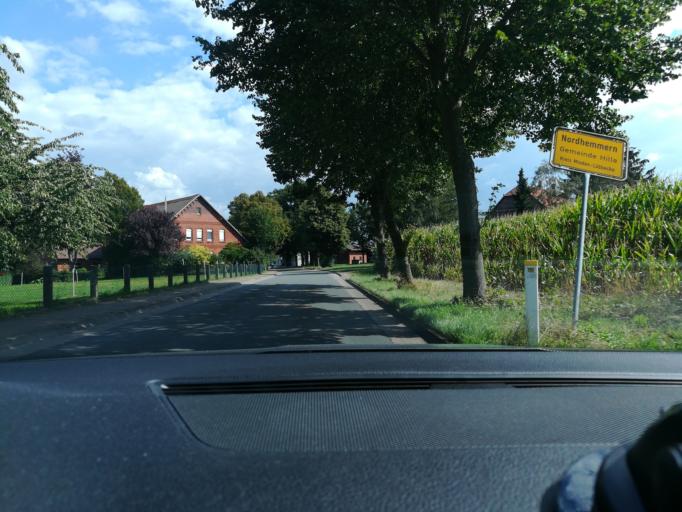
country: DE
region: North Rhine-Westphalia
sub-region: Regierungsbezirk Detmold
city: Hille
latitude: 52.3373
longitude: 8.7948
